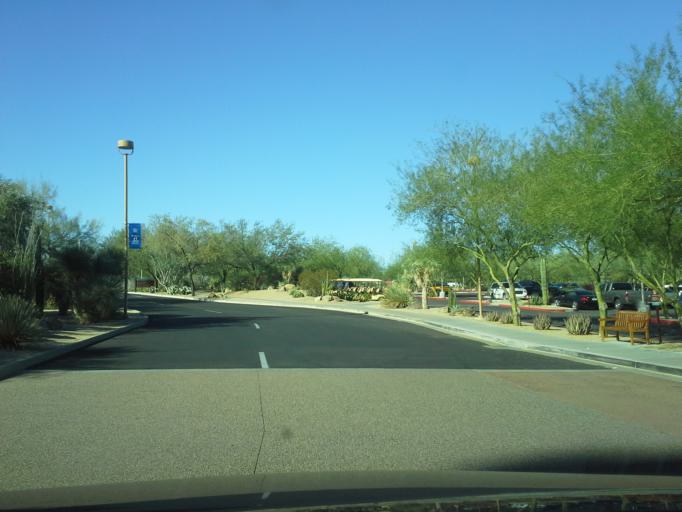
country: US
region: Arizona
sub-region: Maricopa County
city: Paradise Valley
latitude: 33.6595
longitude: -111.9560
